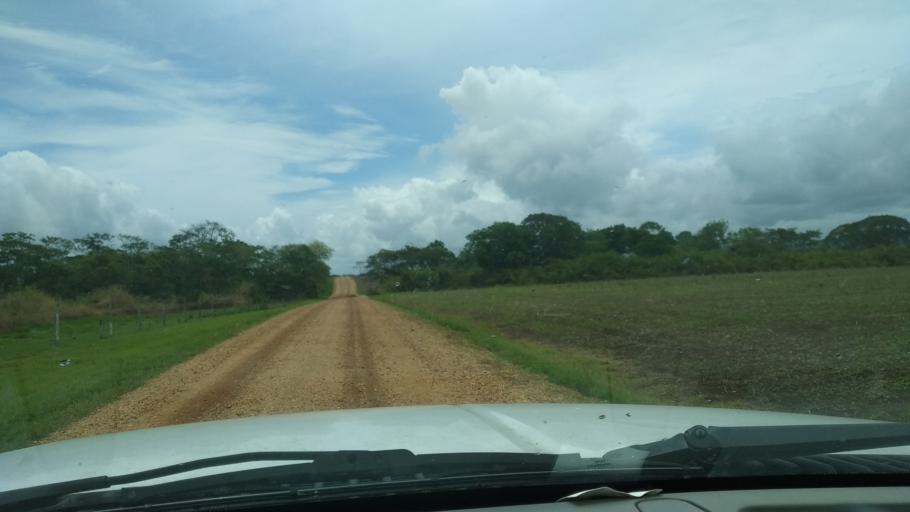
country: BZ
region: Cayo
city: San Ignacio
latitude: 17.2263
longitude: -88.9764
